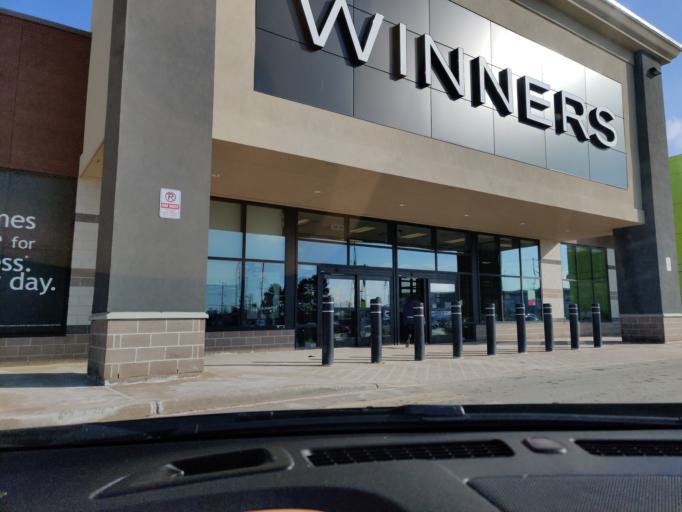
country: CA
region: Ontario
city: Collingwood
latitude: 44.5031
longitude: -80.2383
